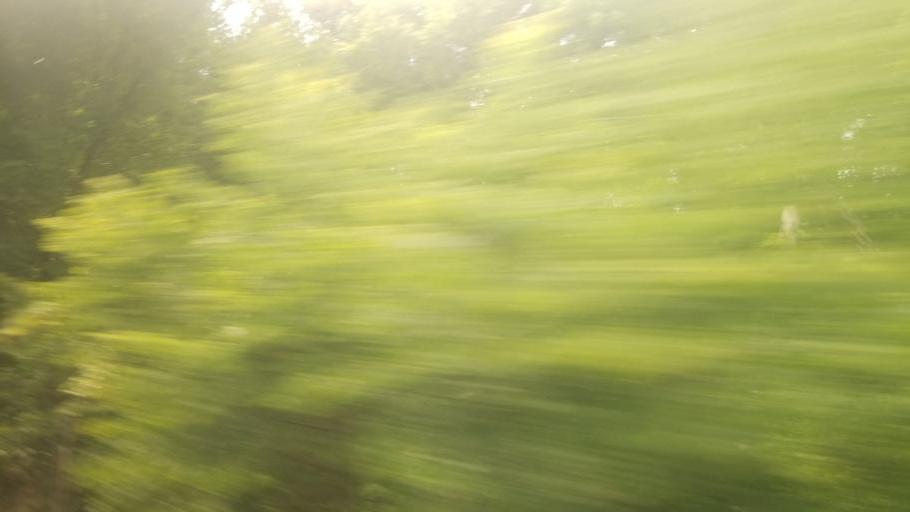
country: US
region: Kansas
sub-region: Douglas County
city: Lawrence
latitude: 38.9499
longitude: -95.1685
